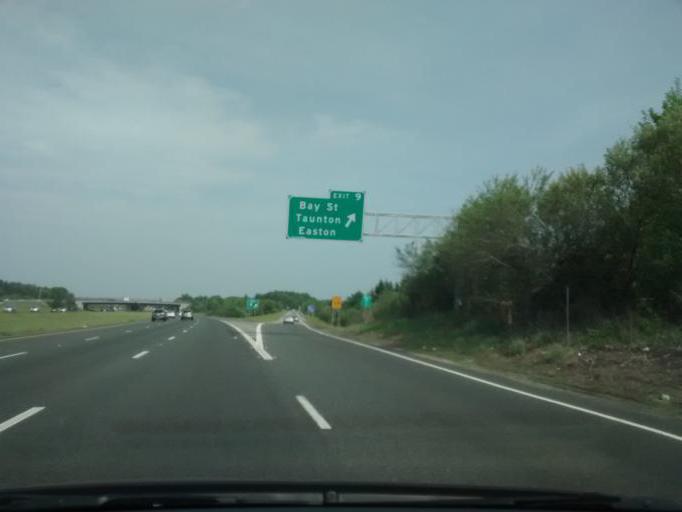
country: US
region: Massachusetts
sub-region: Bristol County
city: Norton Center
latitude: 41.9628
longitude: -71.1302
